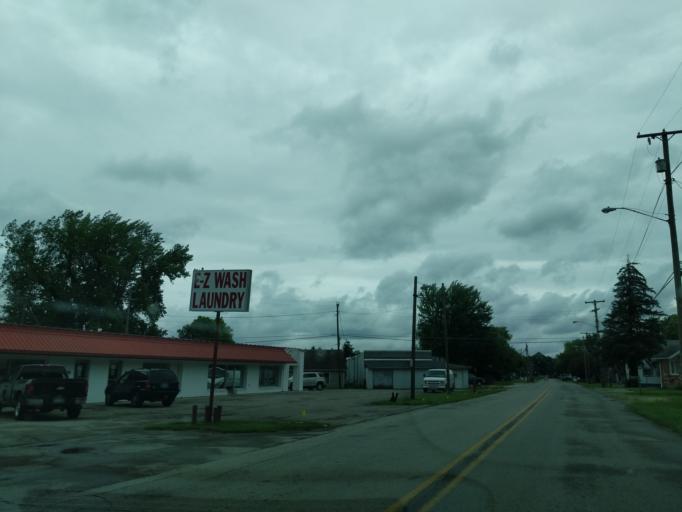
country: US
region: Indiana
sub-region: Madison County
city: Chesterfield
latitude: 40.1101
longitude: -85.6017
